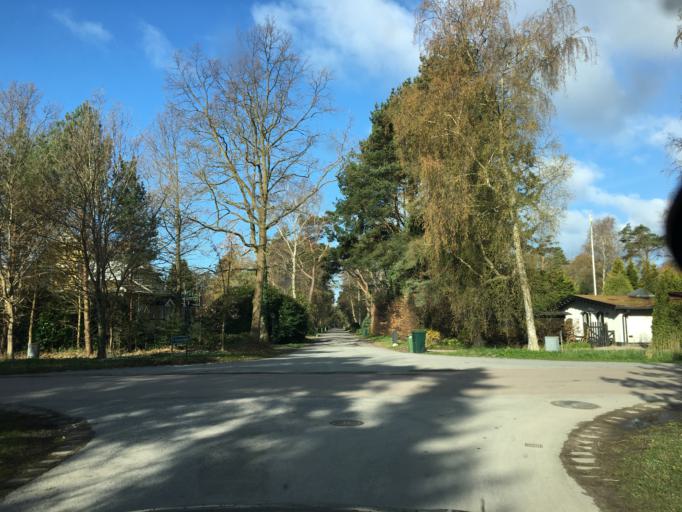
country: SE
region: Skane
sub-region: Vellinge Kommun
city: Ljunghusen
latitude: 55.4040
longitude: 12.9206
